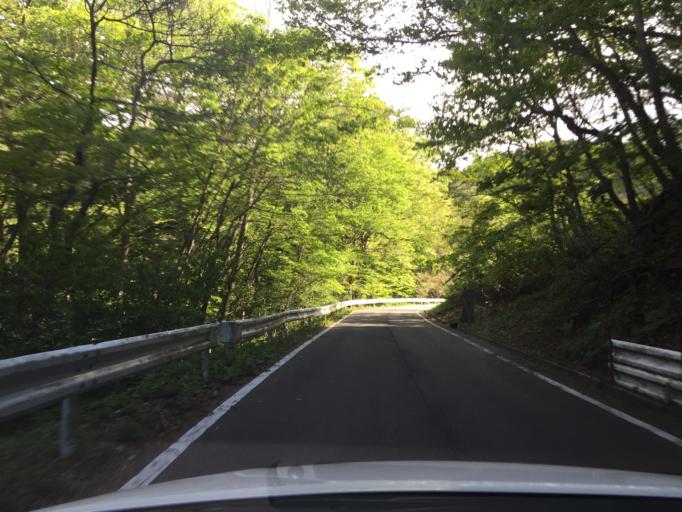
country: JP
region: Miyagi
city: Marumori
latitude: 37.7200
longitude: 140.7852
